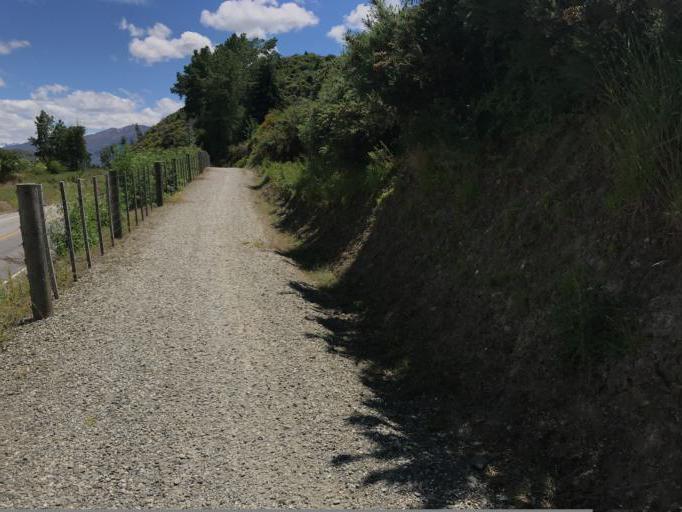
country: NZ
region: Otago
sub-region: Queenstown-Lakes District
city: Arrowtown
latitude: -45.0081
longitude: 168.8853
